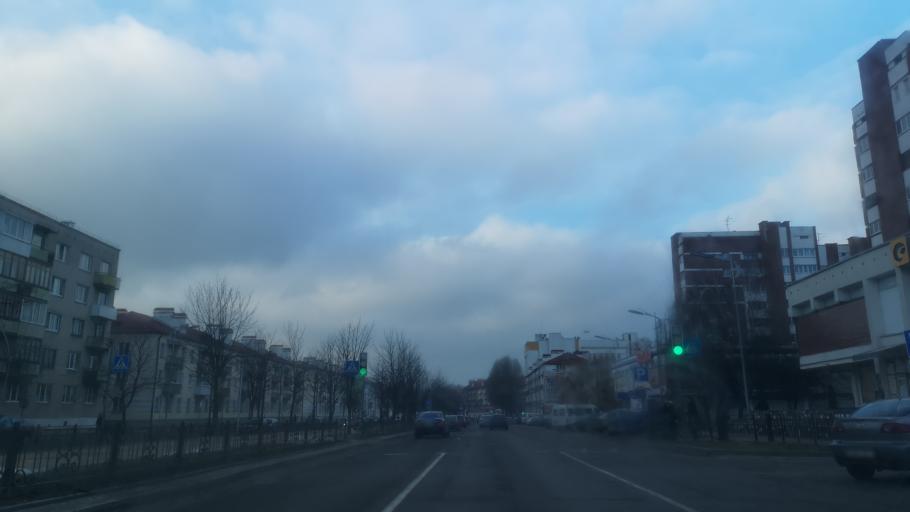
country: BY
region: Brest
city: Brest
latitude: 52.0915
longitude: 23.7011
